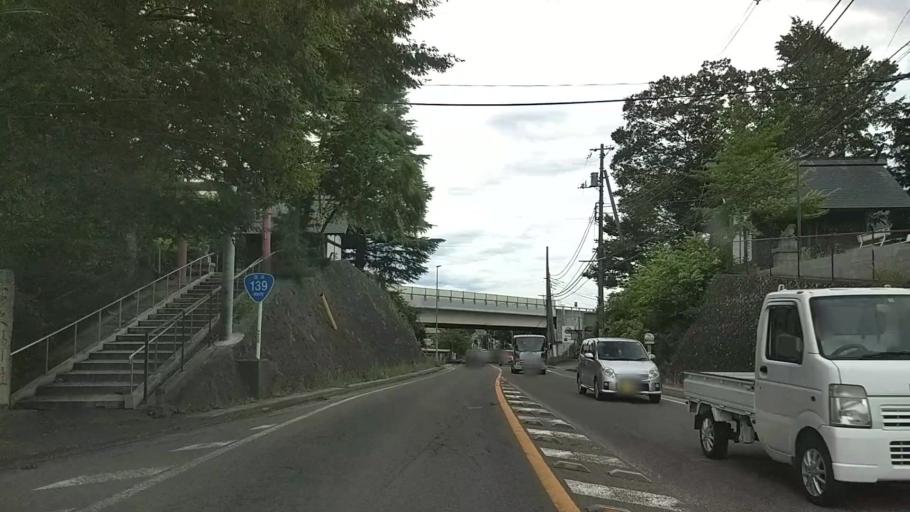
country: JP
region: Yamanashi
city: Fujikawaguchiko
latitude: 35.5040
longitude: 138.8195
